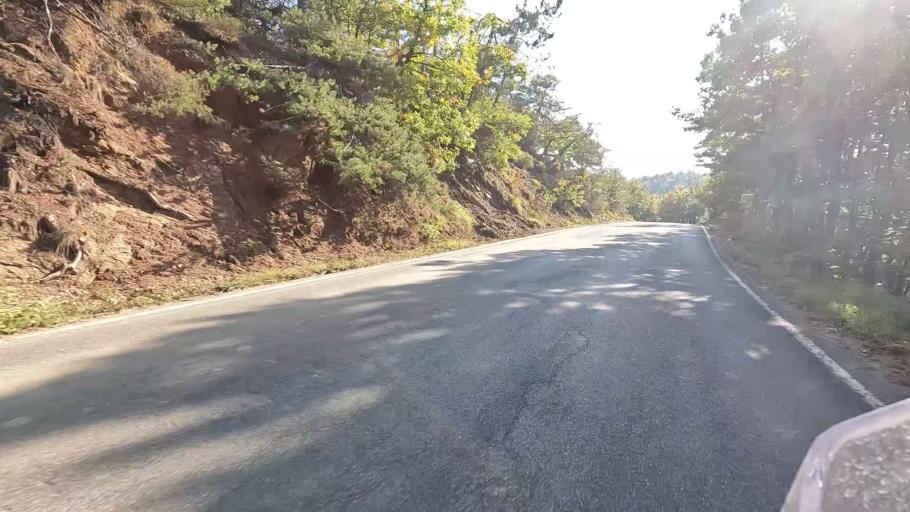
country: IT
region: Liguria
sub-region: Provincia di Savona
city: Urbe
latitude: 44.4996
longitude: 8.5458
